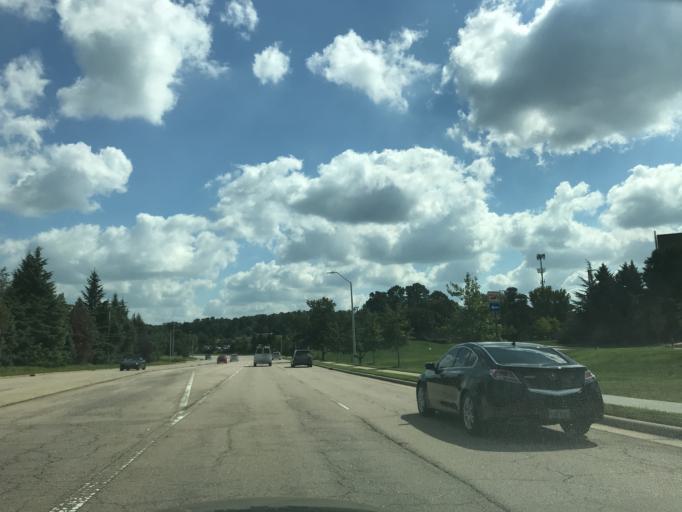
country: US
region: North Carolina
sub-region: Wake County
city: Raleigh
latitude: 35.8659
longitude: -78.5809
